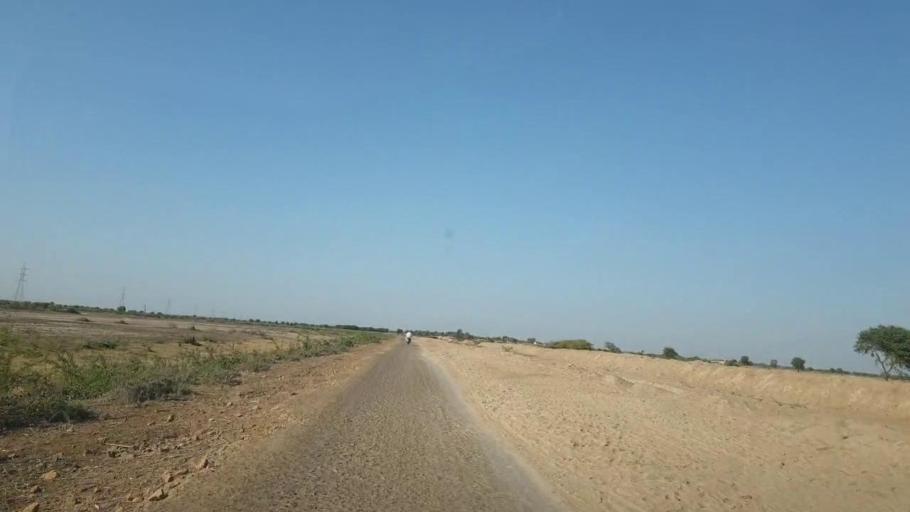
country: PK
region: Sindh
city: Naukot
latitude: 25.0389
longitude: 69.4421
